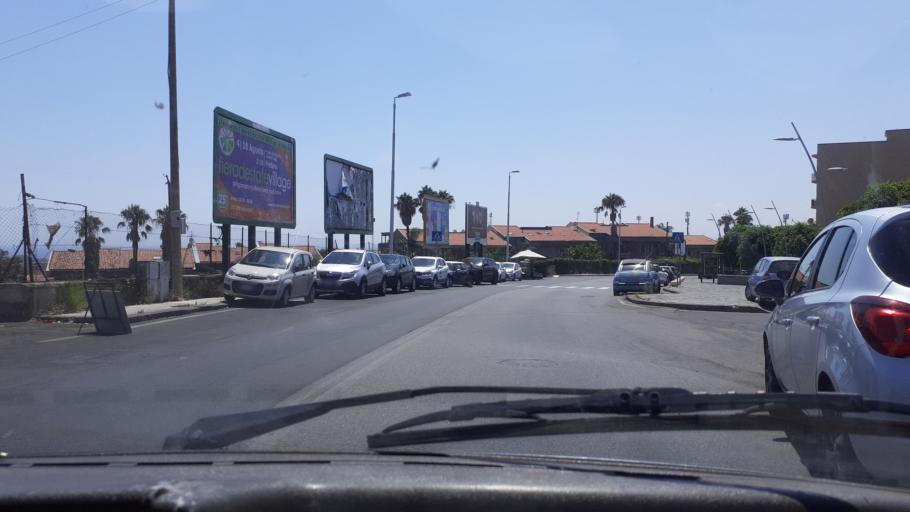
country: IT
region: Sicily
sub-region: Catania
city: Cerza
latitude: 37.5382
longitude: 15.1025
